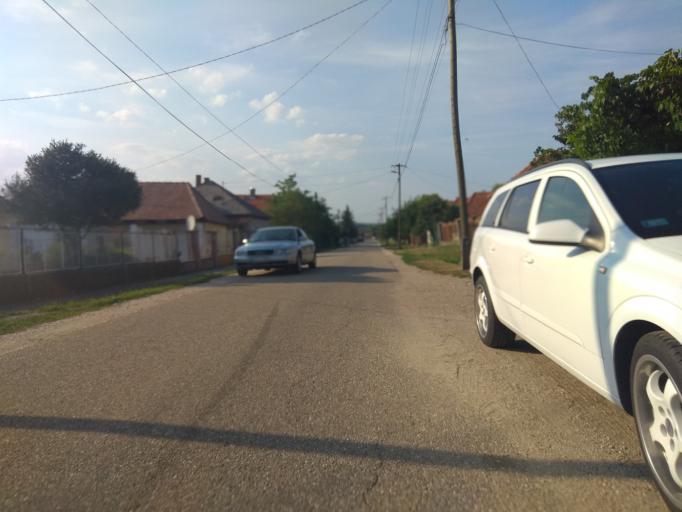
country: HU
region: Borsod-Abauj-Zemplen
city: Harsany
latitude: 47.9182
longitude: 20.7402
